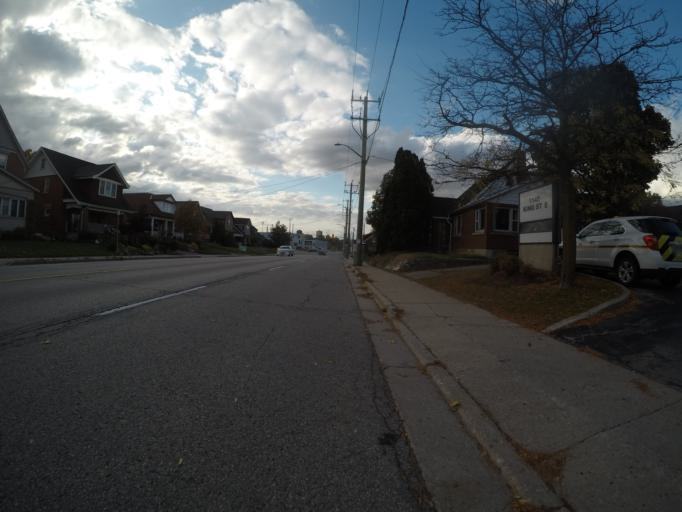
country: CA
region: Ontario
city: Kitchener
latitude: 43.4410
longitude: -80.4717
